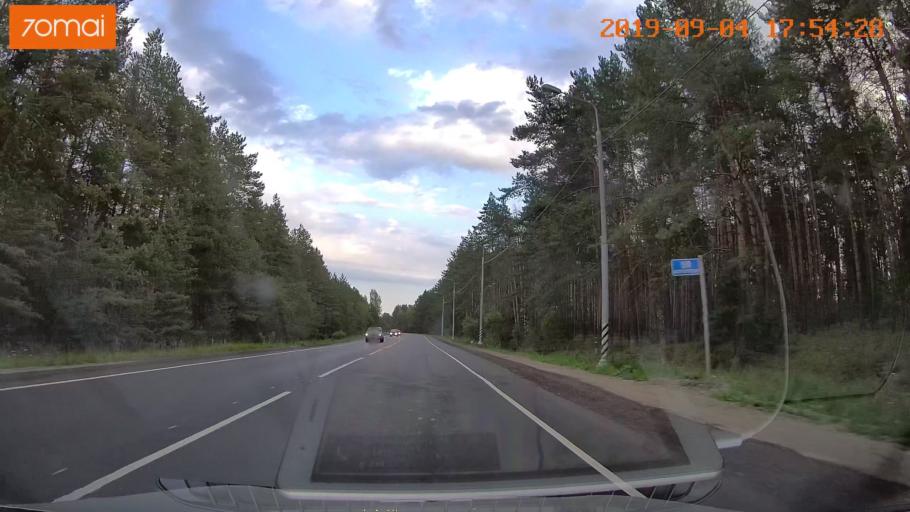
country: RU
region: Moskovskaya
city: Imeni Tsyurupy
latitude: 55.5102
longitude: 38.7459
